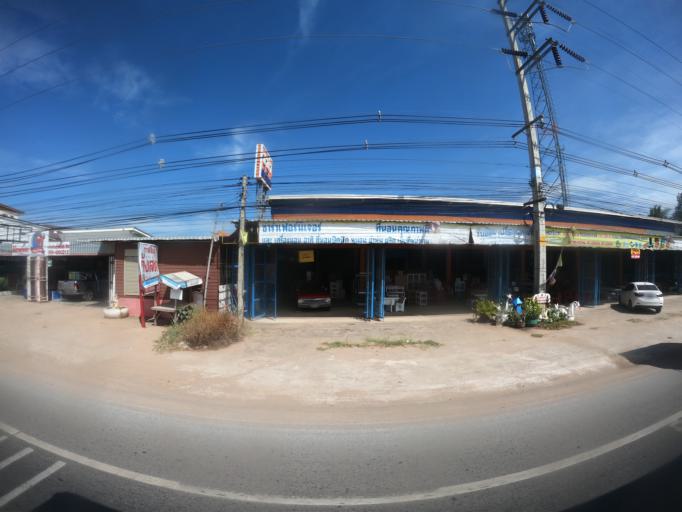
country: TH
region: Khon Kaen
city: Khon Kaen
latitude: 16.4379
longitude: 102.9412
